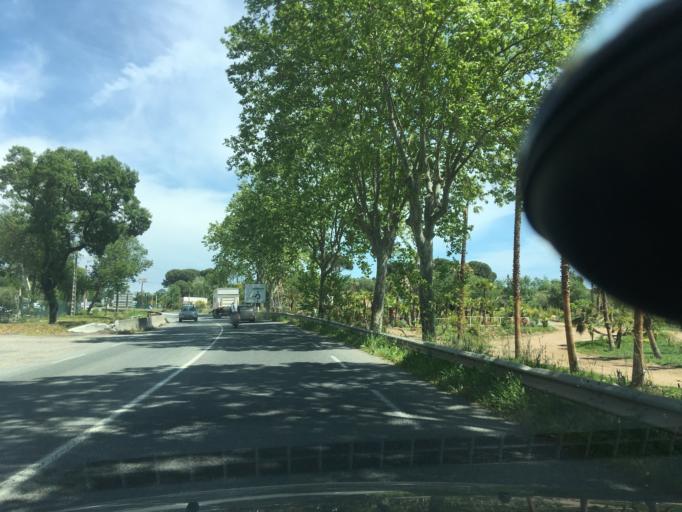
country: FR
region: Provence-Alpes-Cote d'Azur
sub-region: Departement du Var
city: Puget-sur-Argens
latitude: 43.4617
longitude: 6.6529
